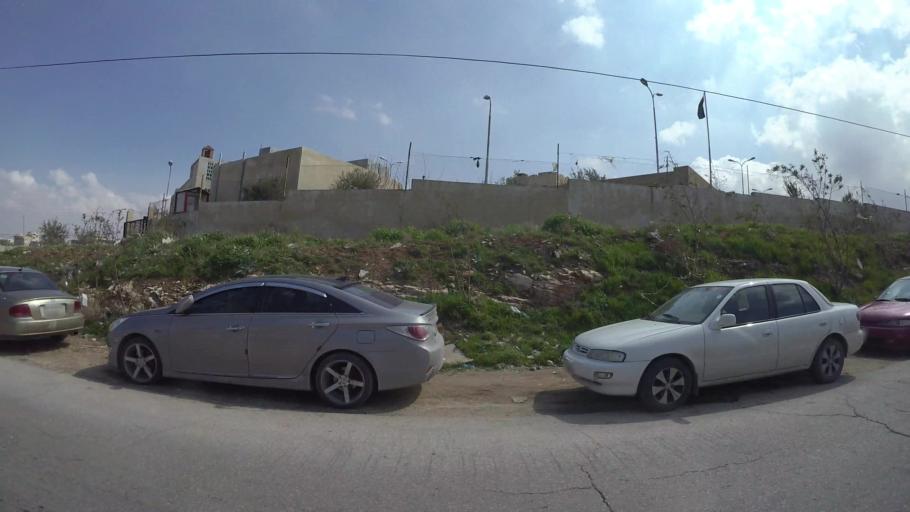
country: JO
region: Zarqa
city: Russeifa
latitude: 31.9972
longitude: 35.9970
